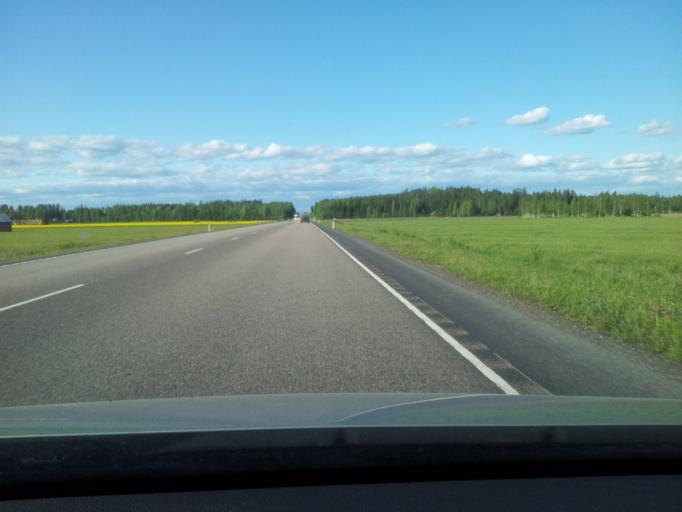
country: FI
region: Kymenlaakso
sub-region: Kouvola
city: Elimaeki
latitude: 60.8005
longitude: 26.5107
